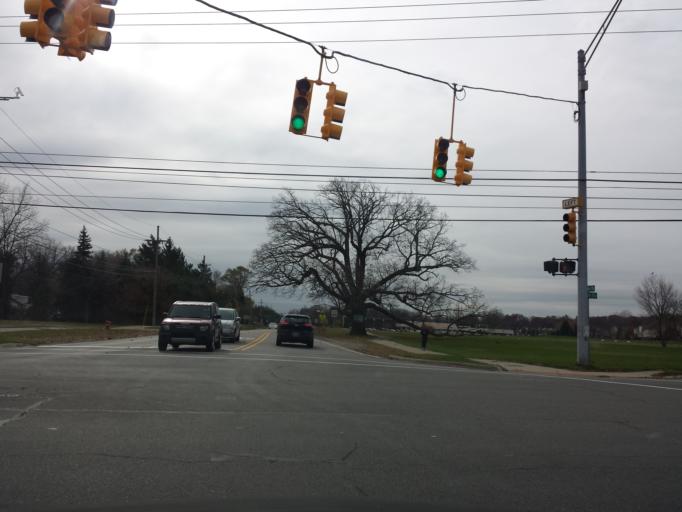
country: US
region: Michigan
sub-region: Oakland County
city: Rochester Hills
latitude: 42.6356
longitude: -83.1521
